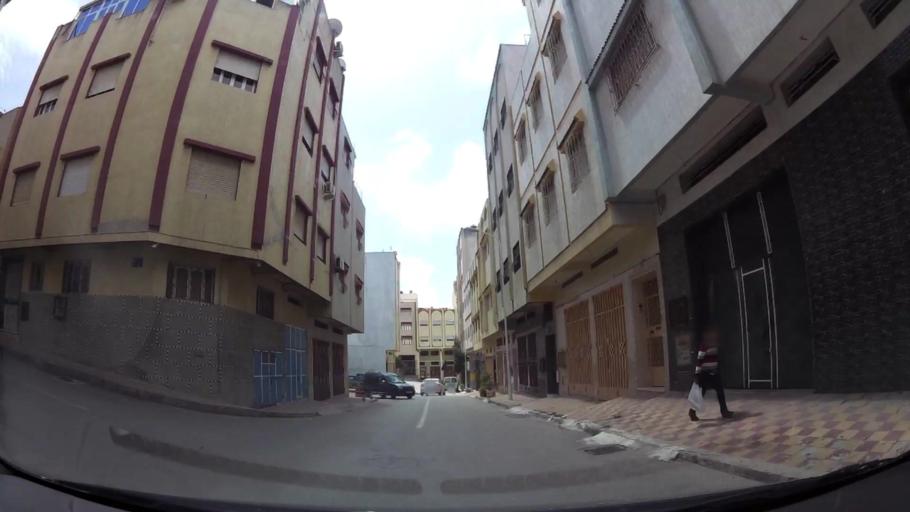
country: MA
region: Tanger-Tetouan
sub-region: Tanger-Assilah
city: Tangier
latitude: 35.7516
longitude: -5.8304
